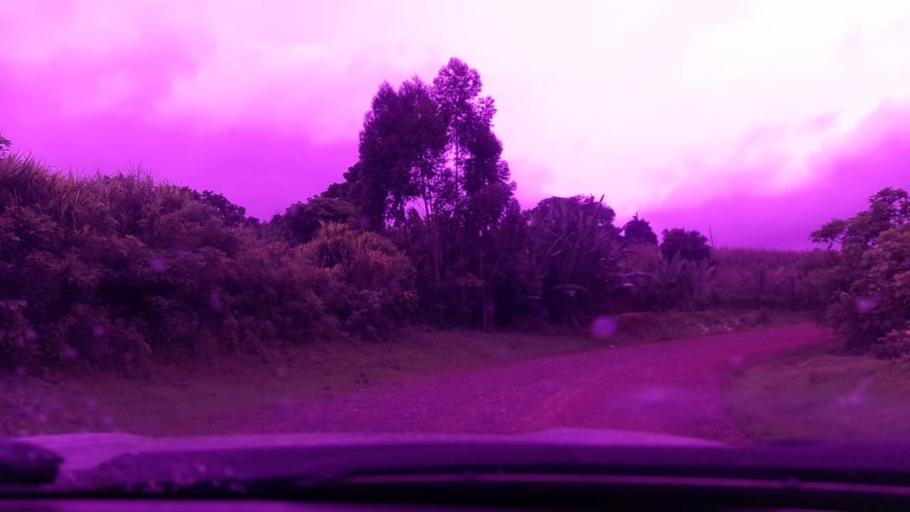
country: ET
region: Southern Nations, Nationalities, and People's Region
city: Tippi
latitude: 7.5633
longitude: 35.7904
